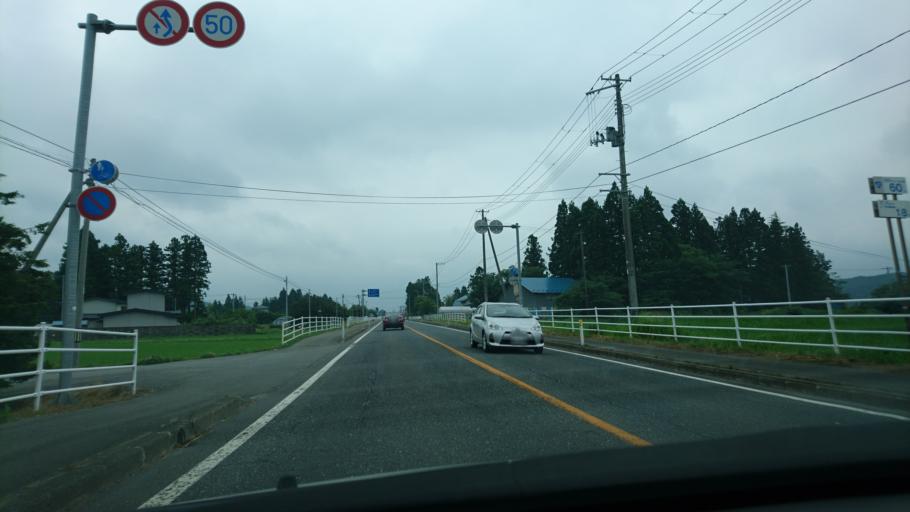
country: JP
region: Miyagi
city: Furukawa
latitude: 38.6999
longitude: 140.8410
